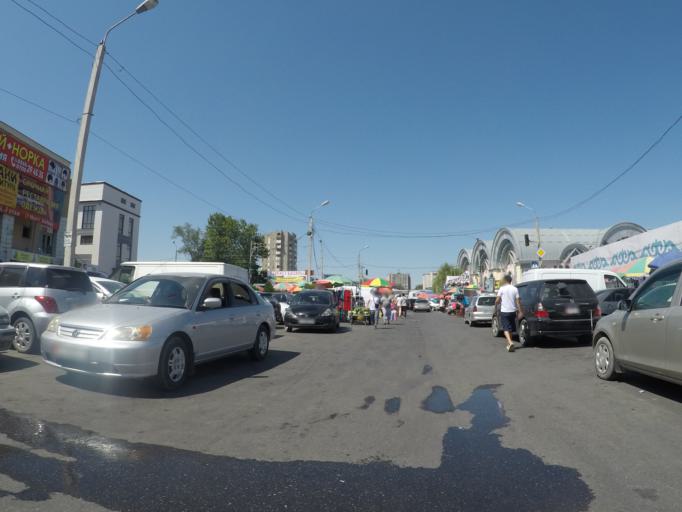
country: KG
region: Chuy
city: Bishkek
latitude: 42.8762
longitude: 74.5691
